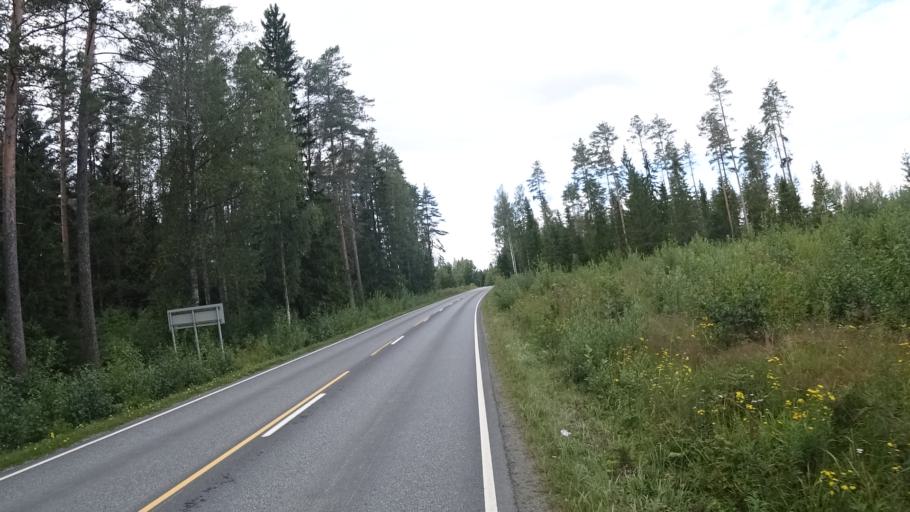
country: FI
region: North Karelia
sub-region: Joensuu
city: Ilomantsi
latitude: 62.6506
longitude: 30.9736
